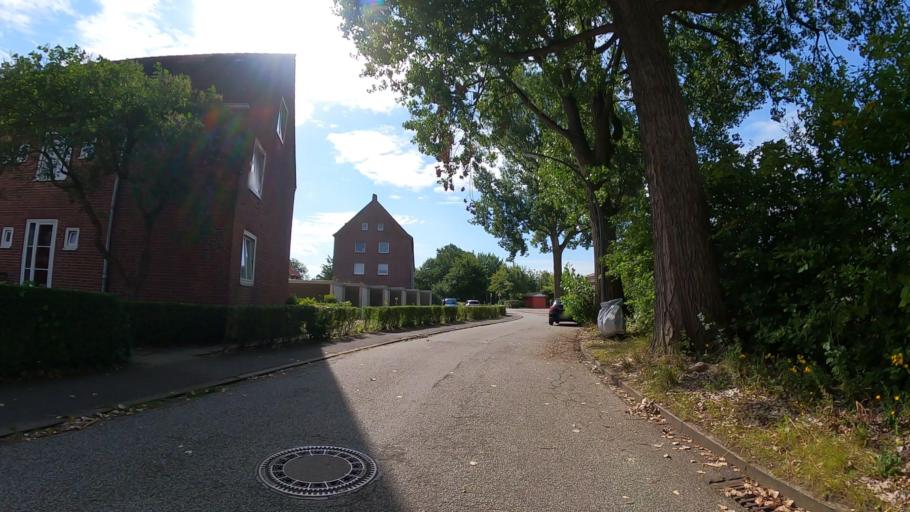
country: DE
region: Hamburg
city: Altona
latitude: 53.5357
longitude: 9.8732
